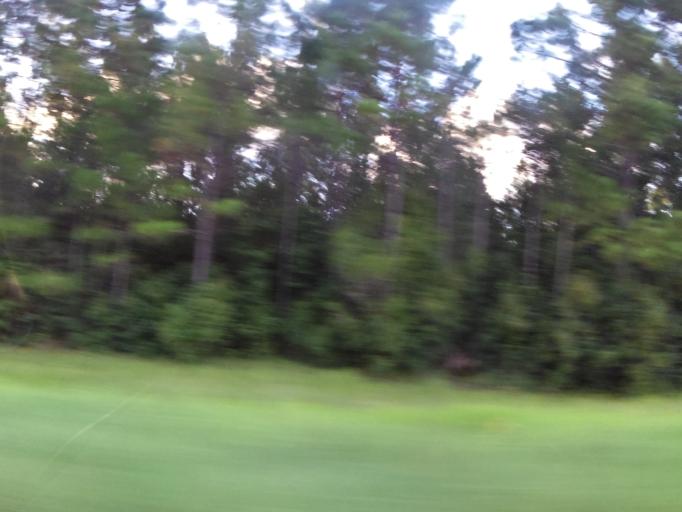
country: US
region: Georgia
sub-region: Camden County
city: Woodbine
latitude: 31.1073
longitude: -81.6708
